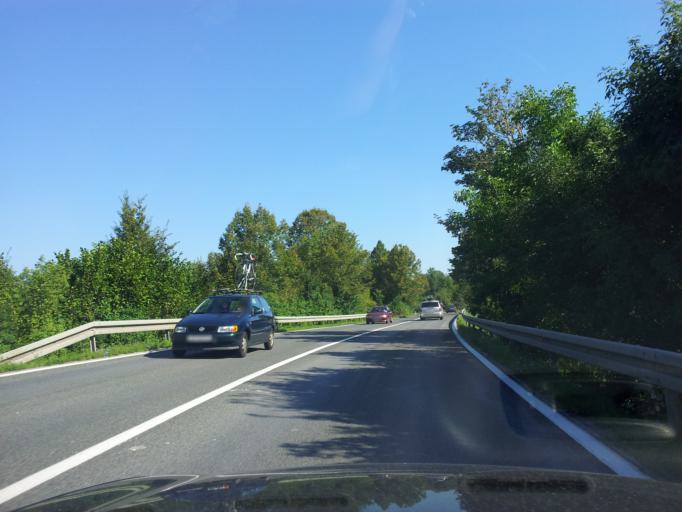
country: HR
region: Karlovacka
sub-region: Grad Karlovac
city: Slunj
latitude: 45.2088
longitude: 15.5449
